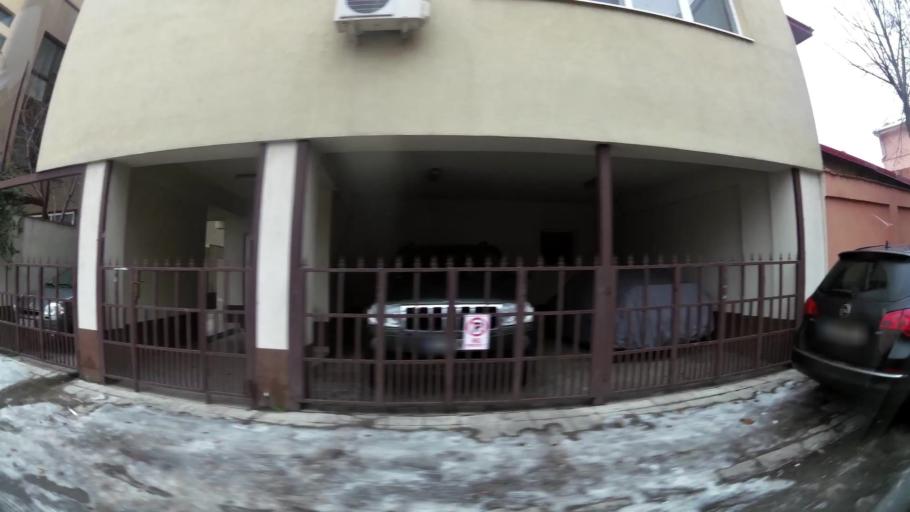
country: RO
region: Bucuresti
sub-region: Municipiul Bucuresti
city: Bucharest
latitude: 44.4512
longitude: 26.1137
